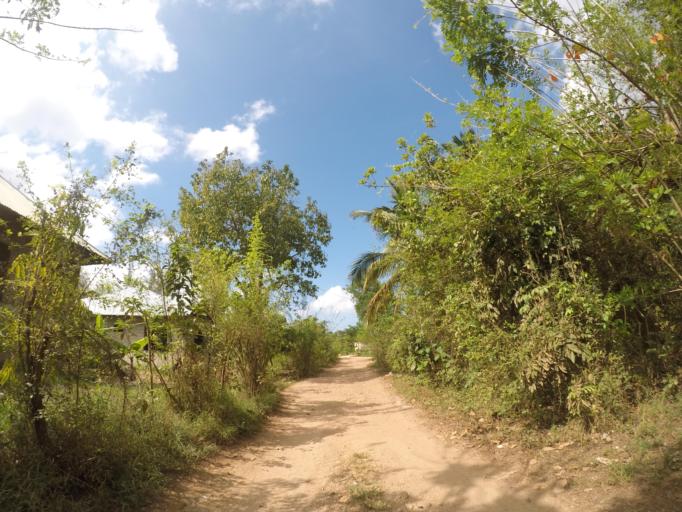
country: TZ
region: Zanzibar Central/South
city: Koani
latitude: -6.1982
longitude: 39.3160
